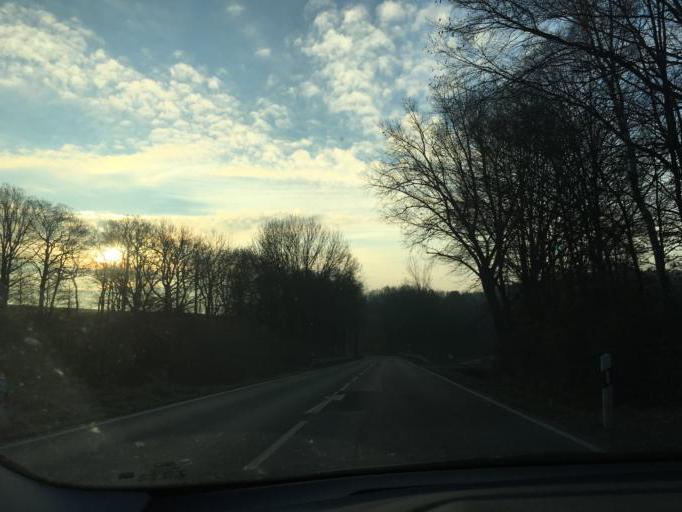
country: DE
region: Saxony
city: Penig
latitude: 50.9366
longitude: 12.6833
